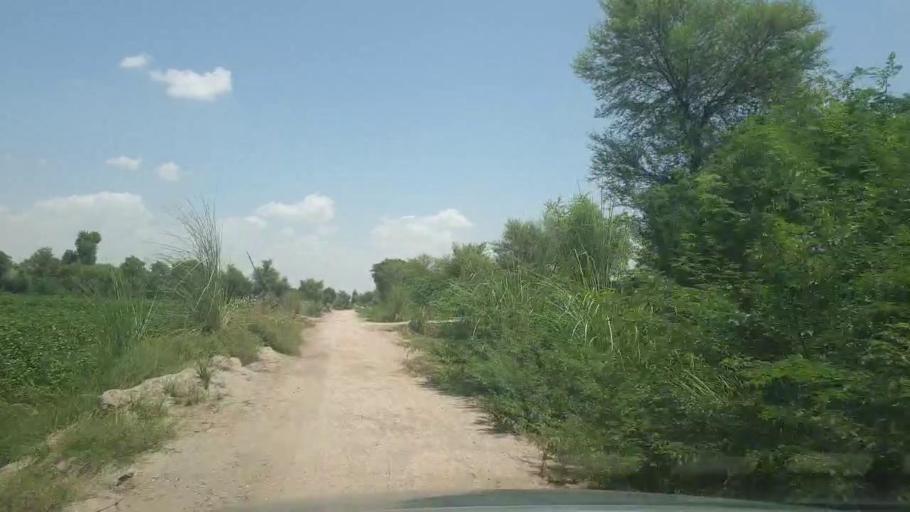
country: PK
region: Sindh
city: Kot Diji
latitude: 27.2635
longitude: 69.0212
